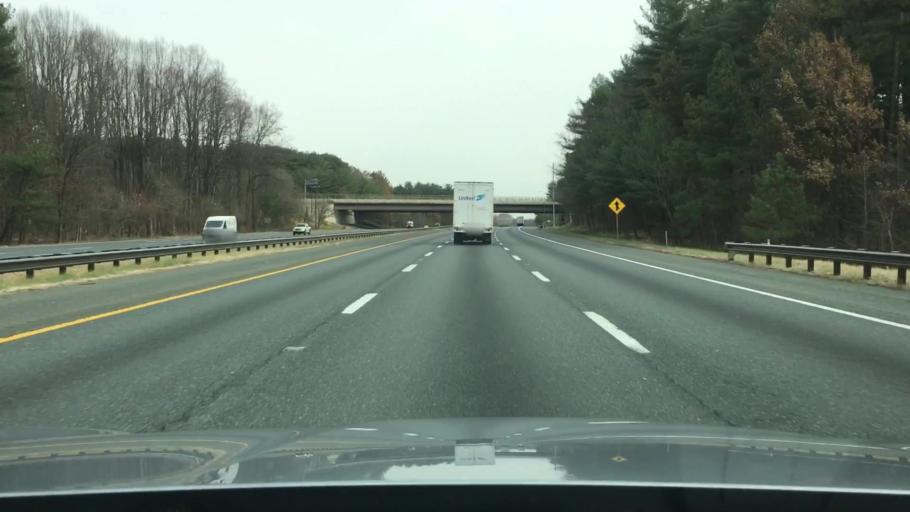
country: US
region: Maryland
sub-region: Anne Arundel County
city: Davidsonville
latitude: 38.9601
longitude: -76.6587
